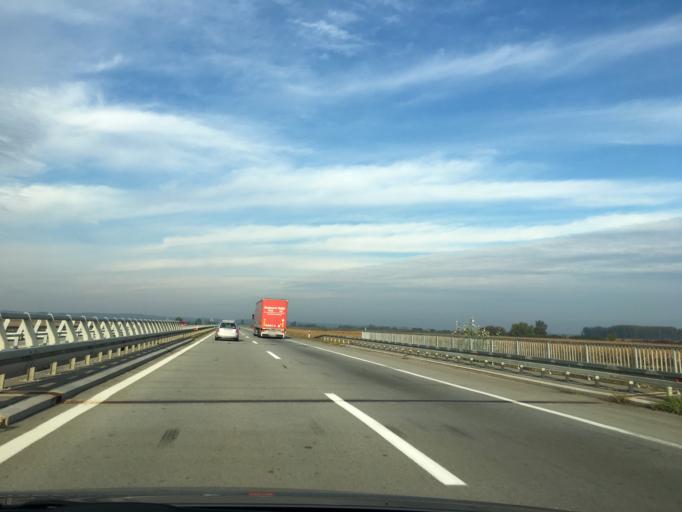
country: RS
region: Autonomna Pokrajina Vojvodina
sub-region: Juznobacki Okrug
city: Kovilj
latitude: 45.2667
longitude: 19.9637
